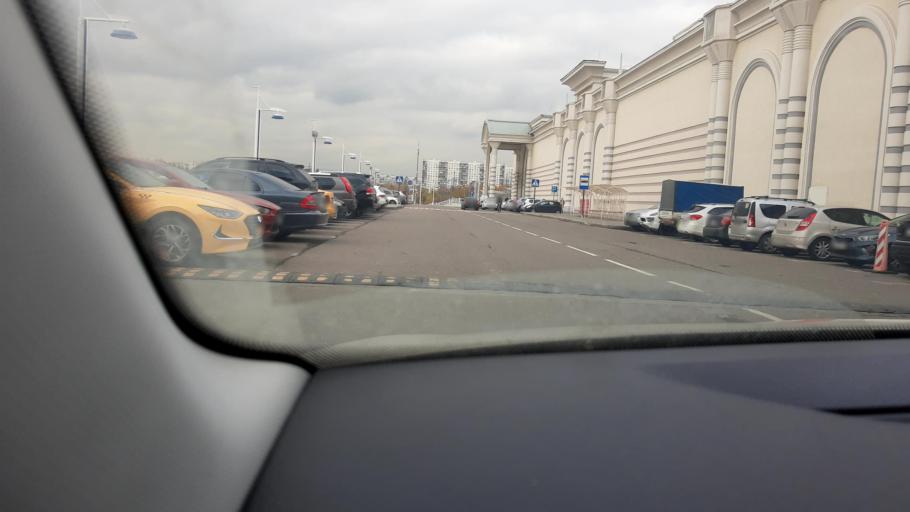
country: RU
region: Moskovskaya
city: Razvilka
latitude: 55.5868
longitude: 37.7235
